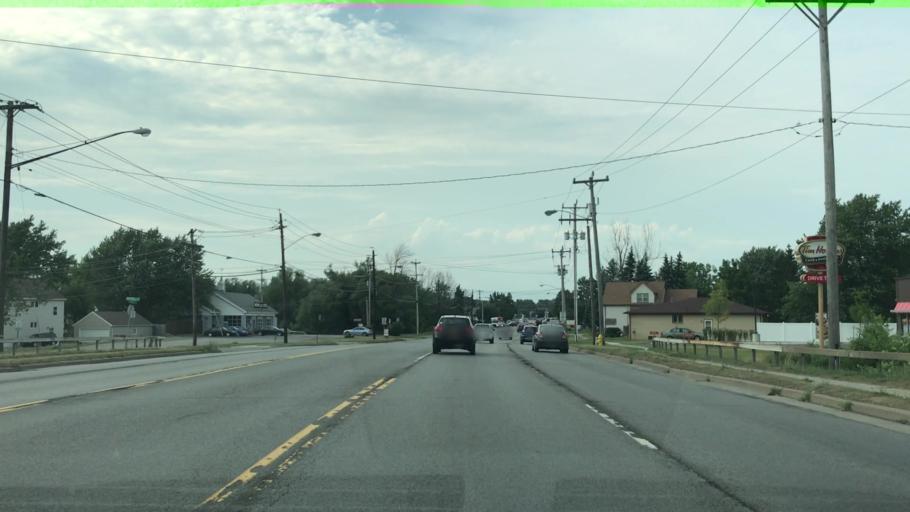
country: US
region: New York
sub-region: Erie County
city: Cheektowaga
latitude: 42.9246
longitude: -78.7418
